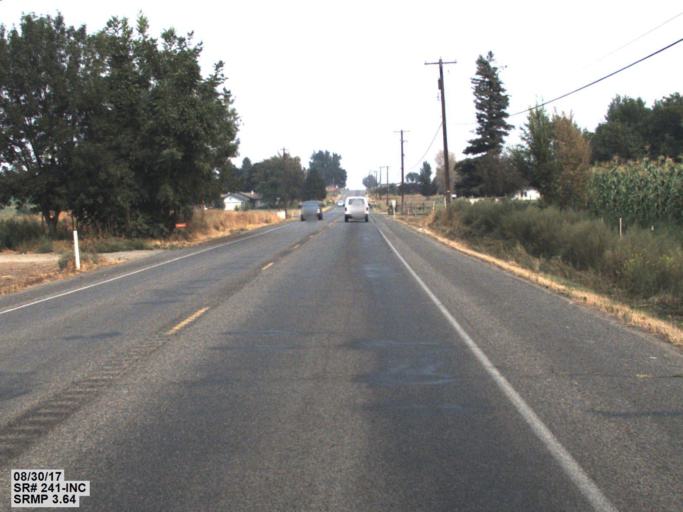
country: US
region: Washington
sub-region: Yakima County
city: Mabton
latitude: 46.2642
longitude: -119.9994
